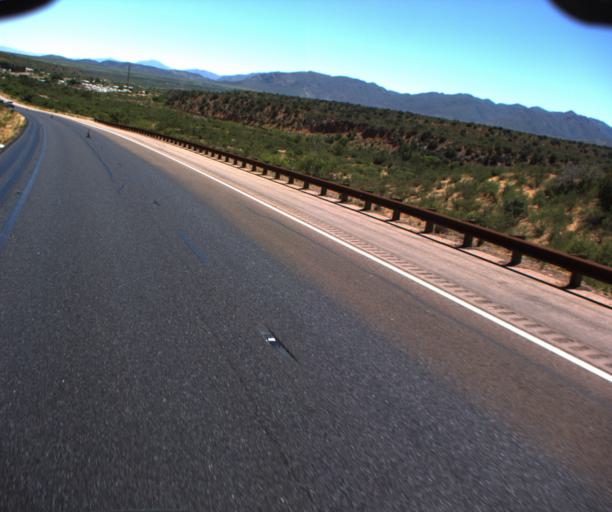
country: US
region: Arizona
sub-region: Gila County
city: Payson
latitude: 34.1183
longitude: -111.3571
